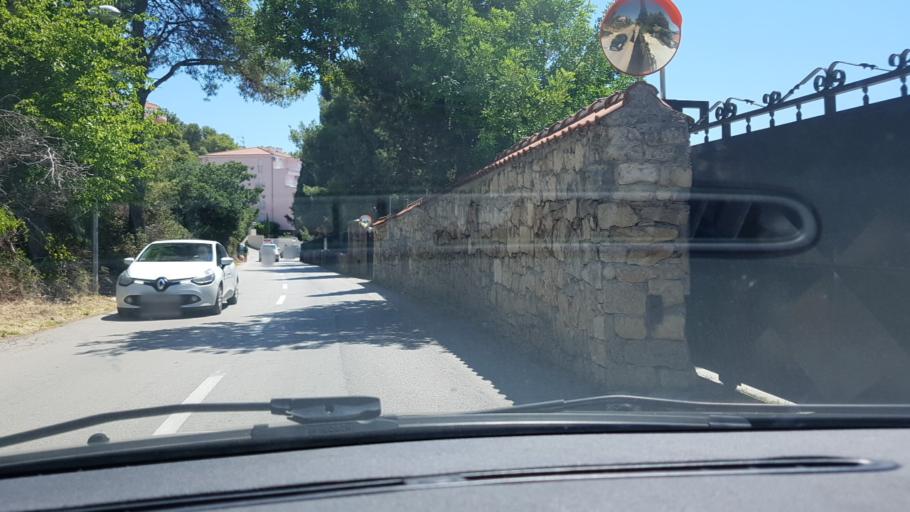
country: HR
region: Splitsko-Dalmatinska
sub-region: Grad Trogir
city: Trogir
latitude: 43.5110
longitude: 16.2534
